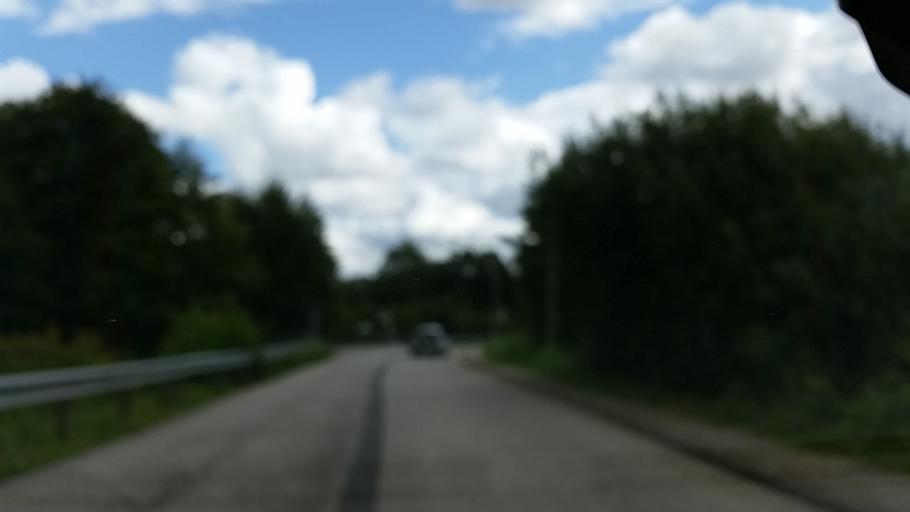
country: DE
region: Schleswig-Holstein
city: Escheburg
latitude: 53.4483
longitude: 10.2934
